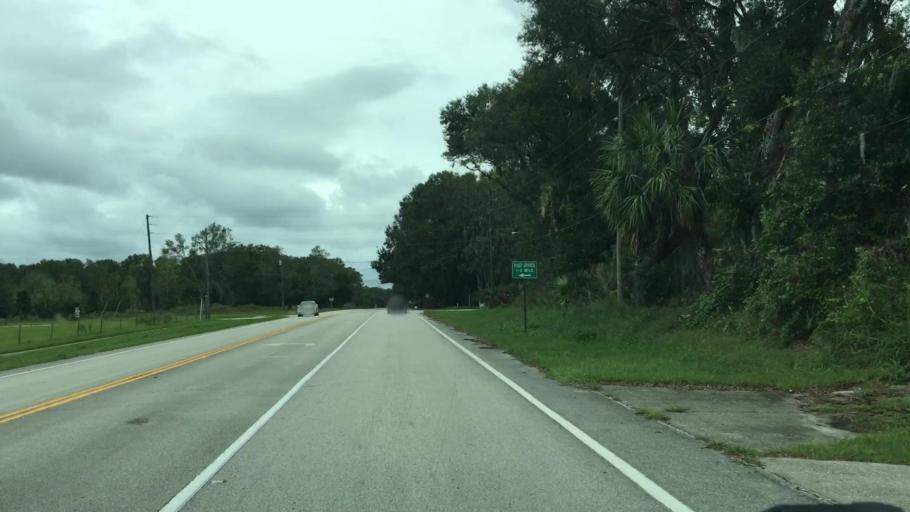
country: US
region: Florida
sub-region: Volusia County
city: Lake Helen
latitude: 28.9841
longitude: -81.2235
